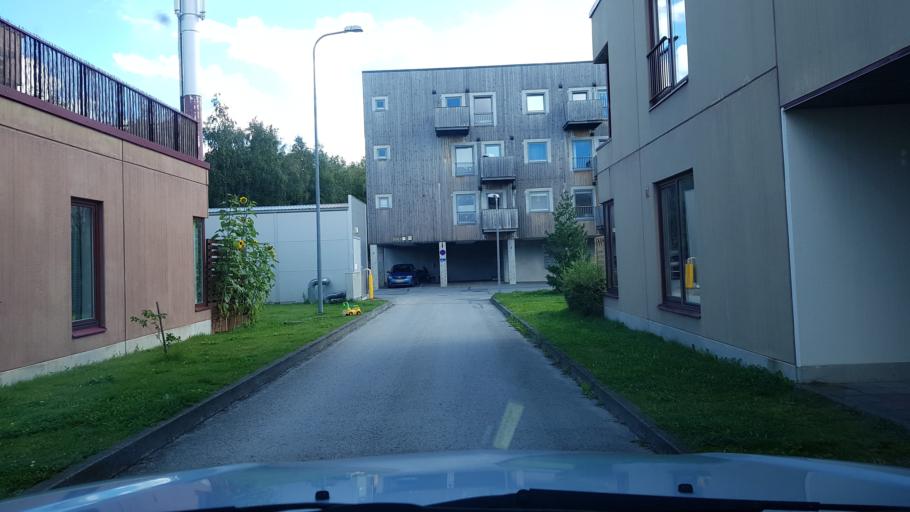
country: EE
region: Harju
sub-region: Tallinna linn
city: Tallinn
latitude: 59.4039
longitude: 24.8044
